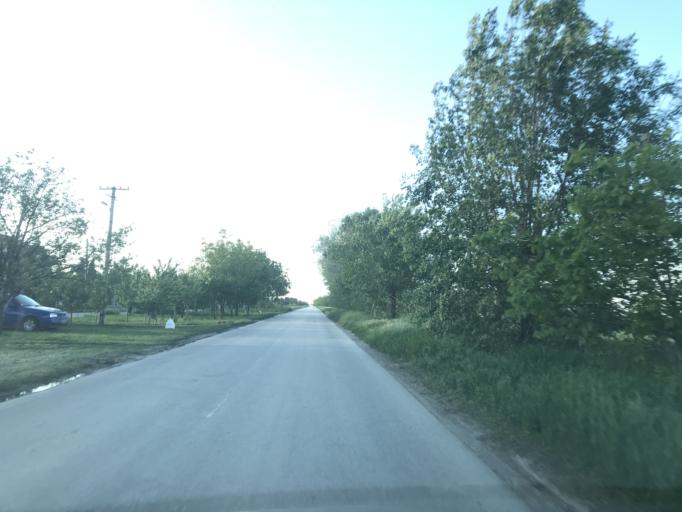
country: RS
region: Autonomna Pokrajina Vojvodina
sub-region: Srednjebanatski Okrug
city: Zrenjanin
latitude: 45.4089
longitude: 20.3928
